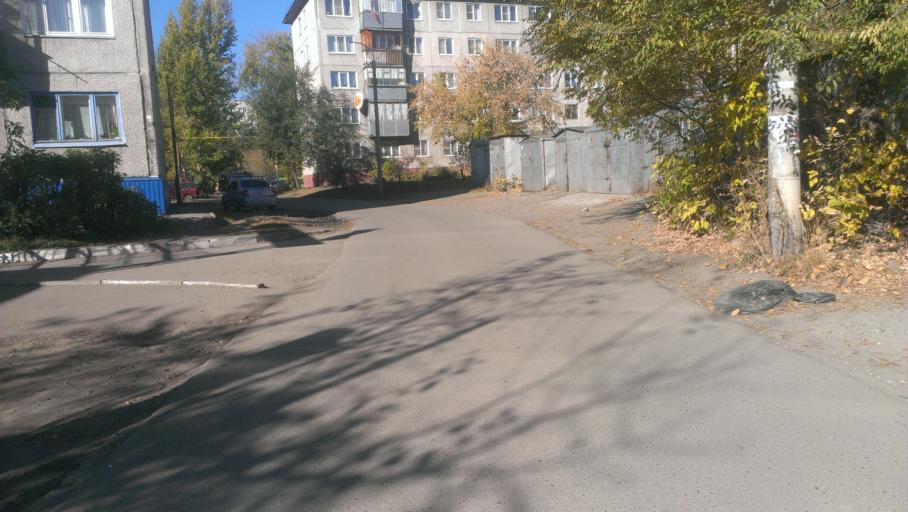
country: RU
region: Altai Krai
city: Novosilikatnyy
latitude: 53.3646
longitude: 83.6788
